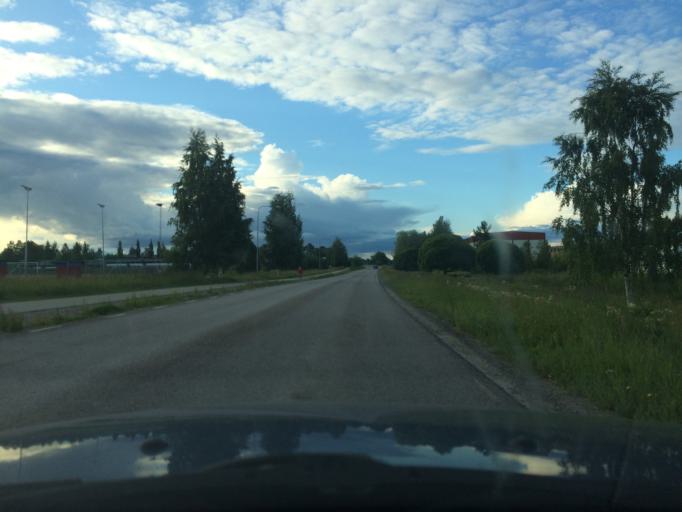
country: SE
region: Norrbotten
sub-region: Pitea Kommun
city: Bergsviken
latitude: 65.3418
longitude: 21.4064
